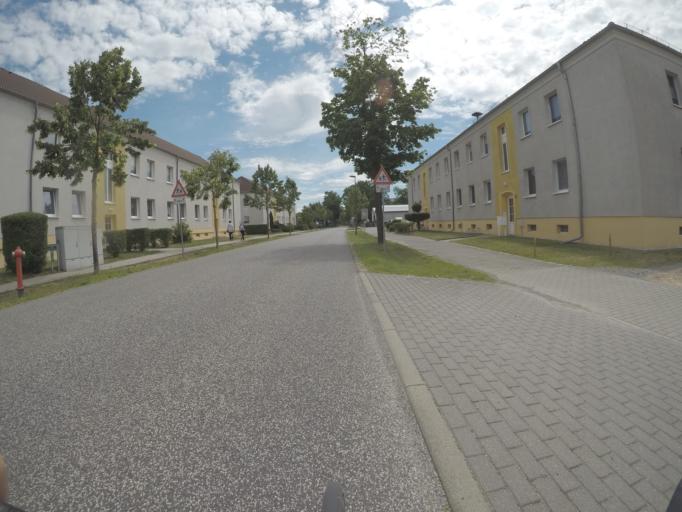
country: DE
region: Brandenburg
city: Storkow
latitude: 52.2496
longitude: 13.9436
